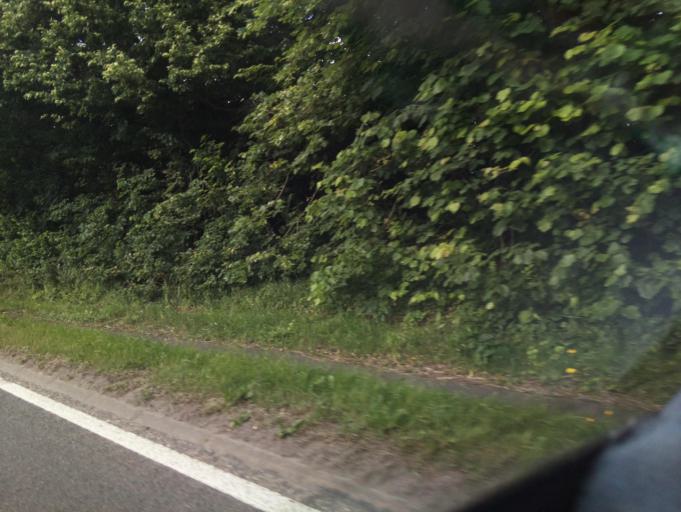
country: GB
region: England
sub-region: Worcestershire
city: Stourport-on-Severn
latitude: 52.3008
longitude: -2.2282
